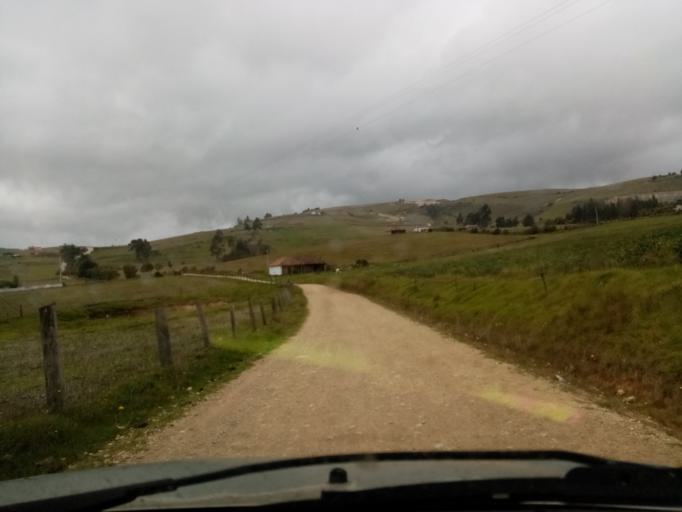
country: CO
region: Boyaca
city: Siachoque
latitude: 5.5635
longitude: -73.2494
